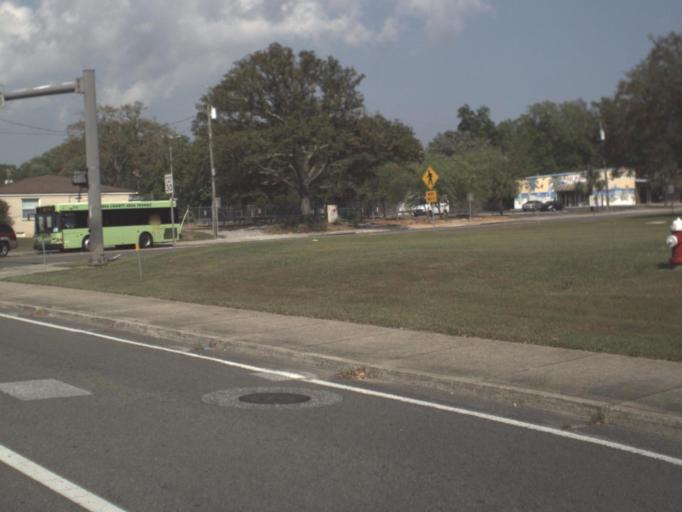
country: US
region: Florida
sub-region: Escambia County
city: Ferry Pass
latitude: 30.4837
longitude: -87.2023
